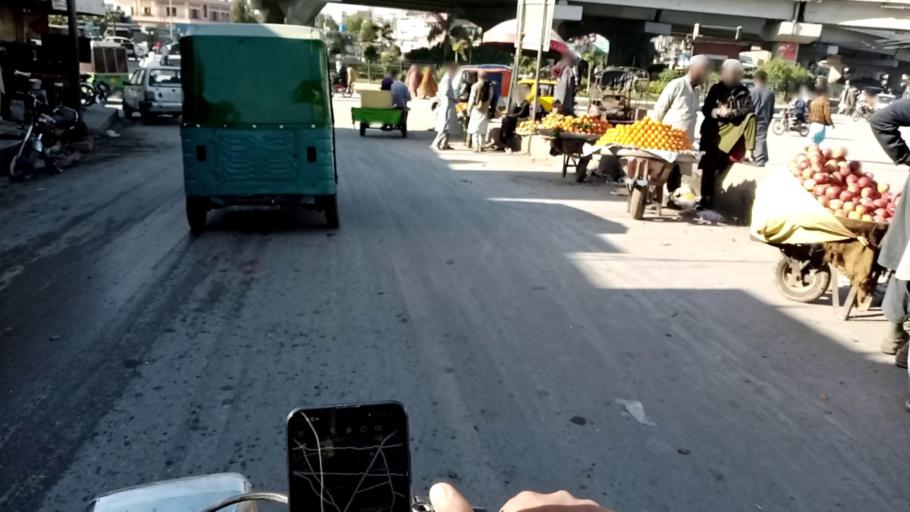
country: PK
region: Khyber Pakhtunkhwa
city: Peshawar
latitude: 34.0166
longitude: 71.5715
